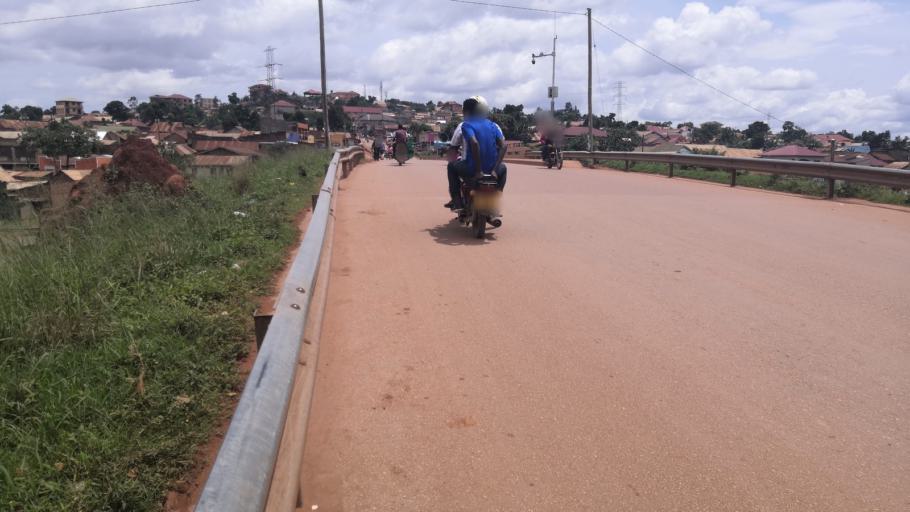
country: UG
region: Central Region
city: Kampala Central Division
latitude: 0.3477
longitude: 32.5535
